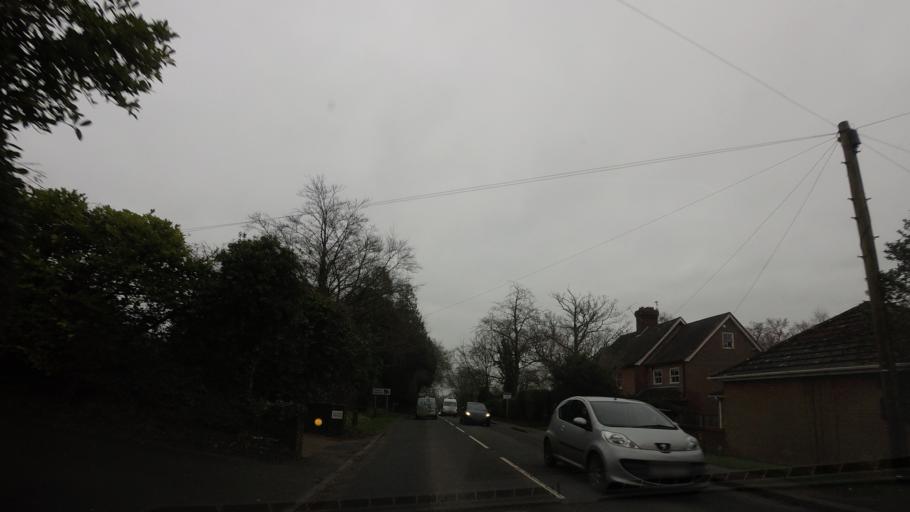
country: GB
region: England
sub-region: Kent
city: Cranbrook
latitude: 51.0903
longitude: 0.5179
